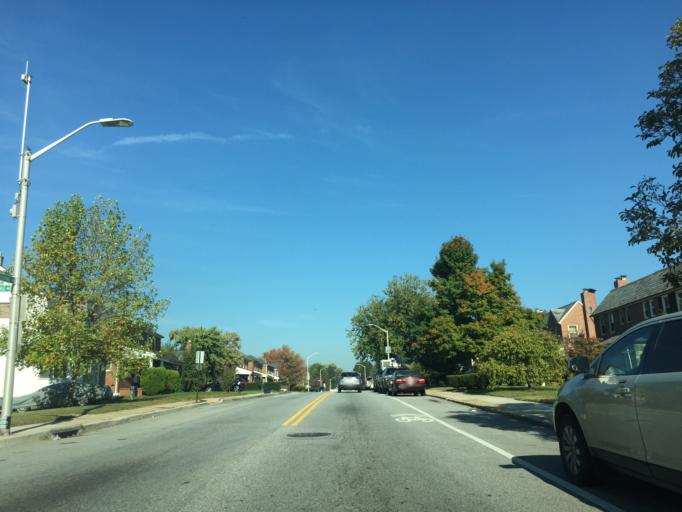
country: US
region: Maryland
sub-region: Baltimore County
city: Parkville
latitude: 39.3424
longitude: -76.5558
